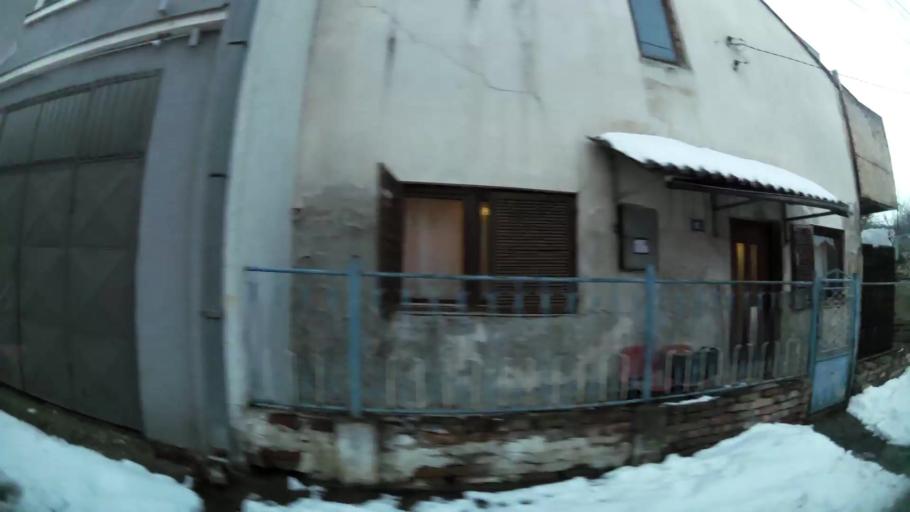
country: RS
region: Central Serbia
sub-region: Belgrade
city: Palilula
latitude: 44.8013
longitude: 20.4996
